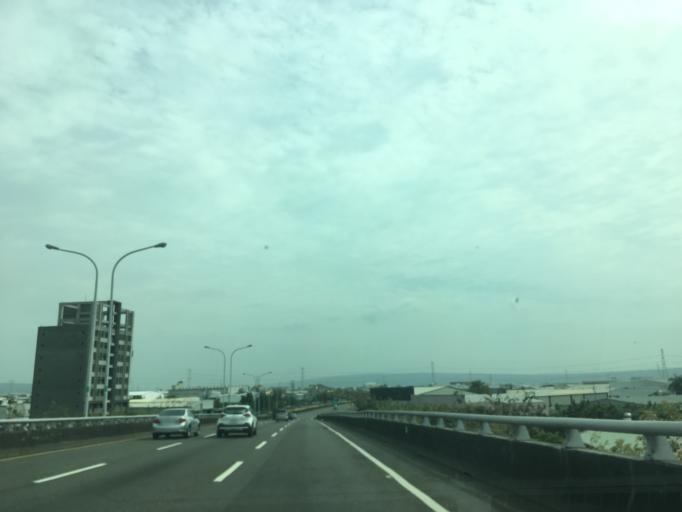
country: TW
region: Taiwan
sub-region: Taichung City
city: Taichung
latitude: 24.0596
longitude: 120.6627
